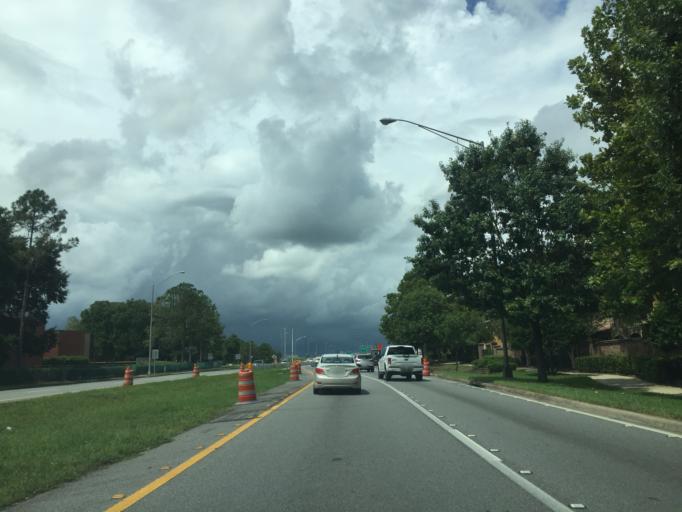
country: US
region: Florida
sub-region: Orange County
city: Eatonville
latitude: 28.6310
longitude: -81.3806
